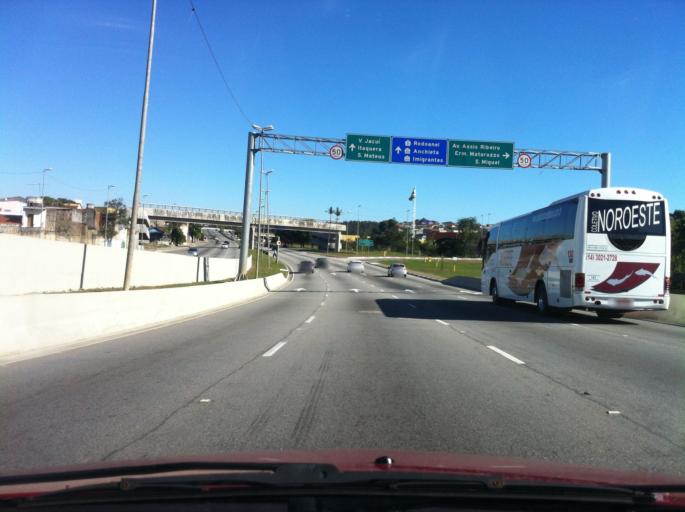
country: BR
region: Sao Paulo
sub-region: Guarulhos
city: Guarulhos
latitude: -23.4936
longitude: -46.4540
